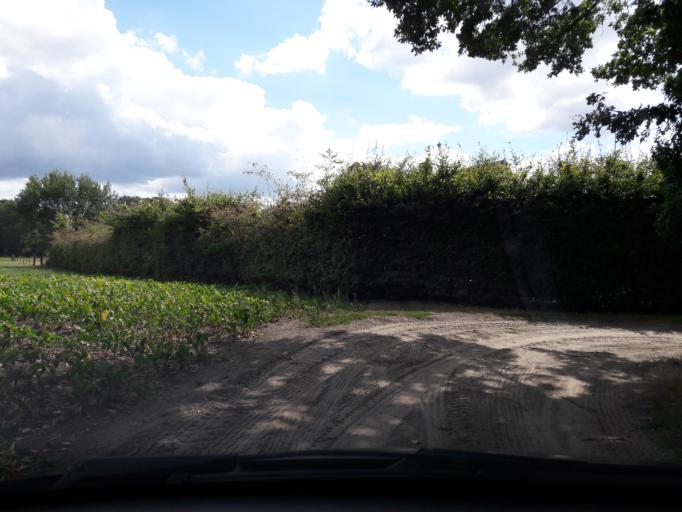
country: NL
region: Drenthe
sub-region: Gemeente Borger-Odoorn
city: Borger
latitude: 52.9545
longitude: 6.7975
